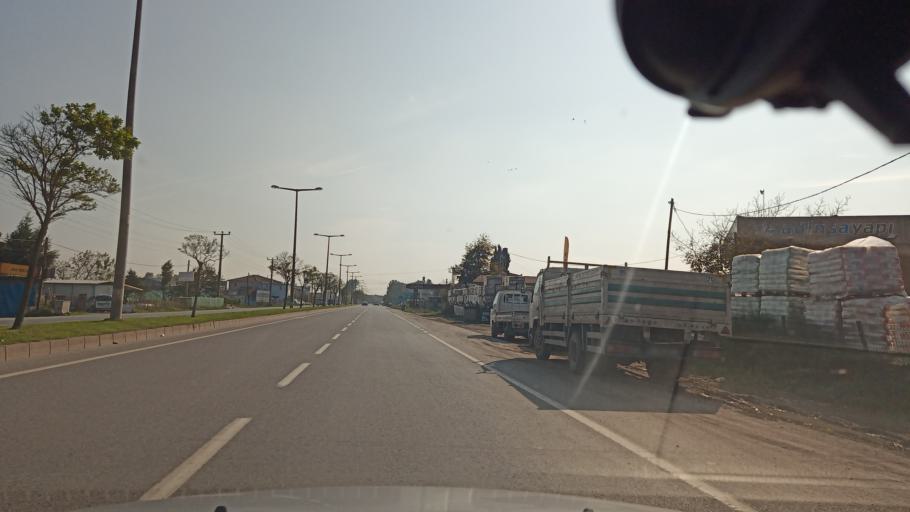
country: TR
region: Sakarya
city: Adapazari
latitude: 40.8179
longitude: 30.4000
